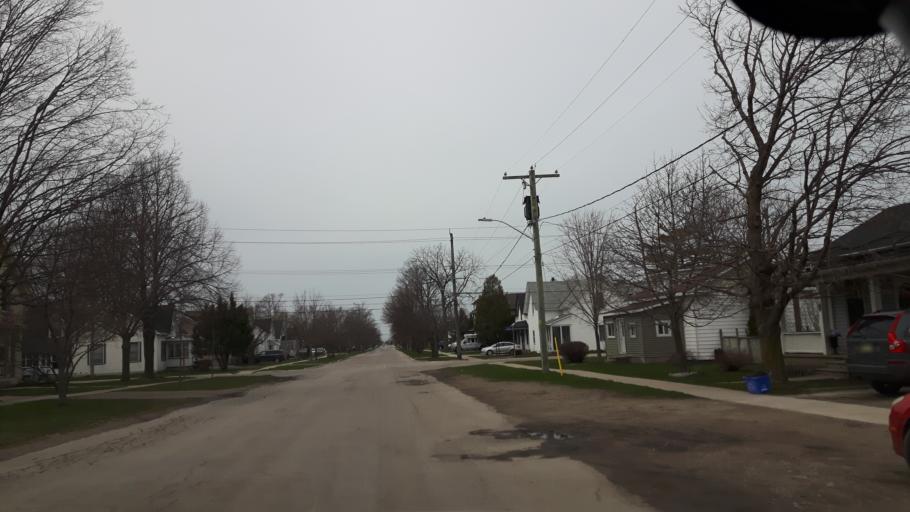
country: CA
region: Ontario
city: Goderich
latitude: 43.7456
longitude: -81.7014
